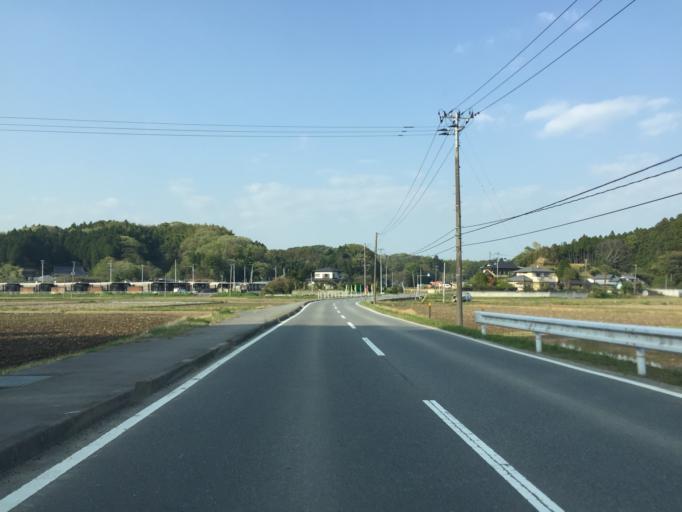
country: JP
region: Fukushima
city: Iwaki
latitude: 36.9630
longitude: 140.8360
